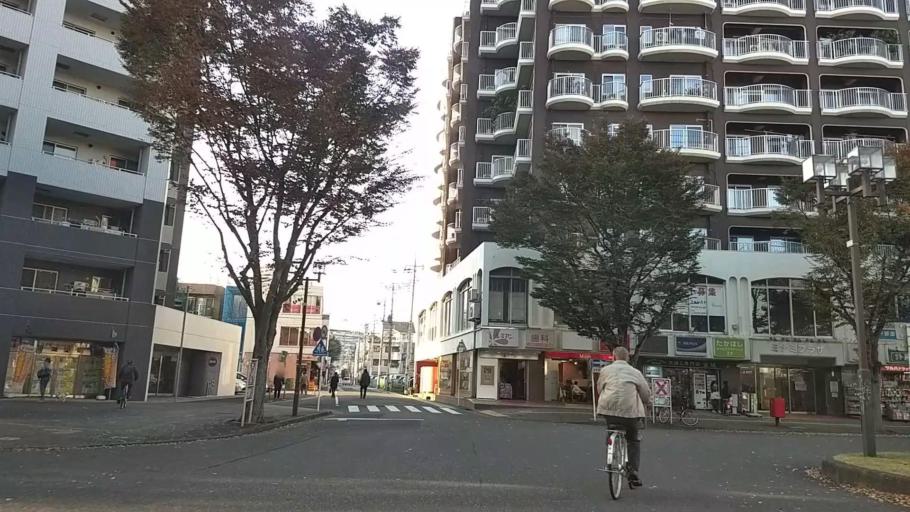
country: JP
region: Saitama
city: Tokorozawa
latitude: 35.8063
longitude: 139.4553
